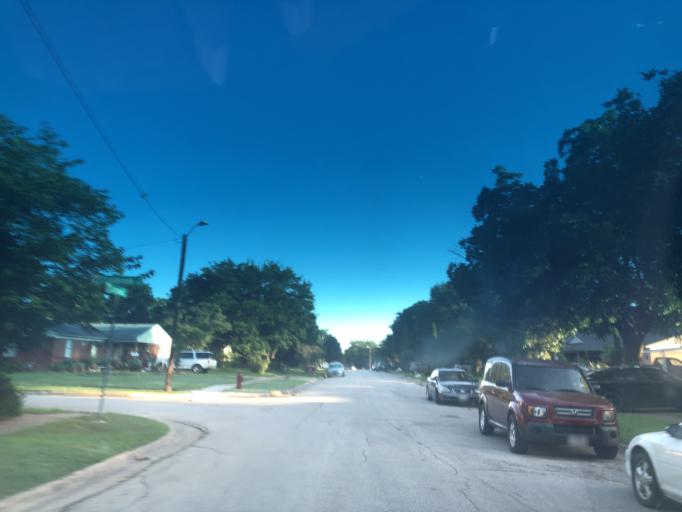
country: US
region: Texas
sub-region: Dallas County
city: Grand Prairie
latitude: 32.7066
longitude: -97.0130
